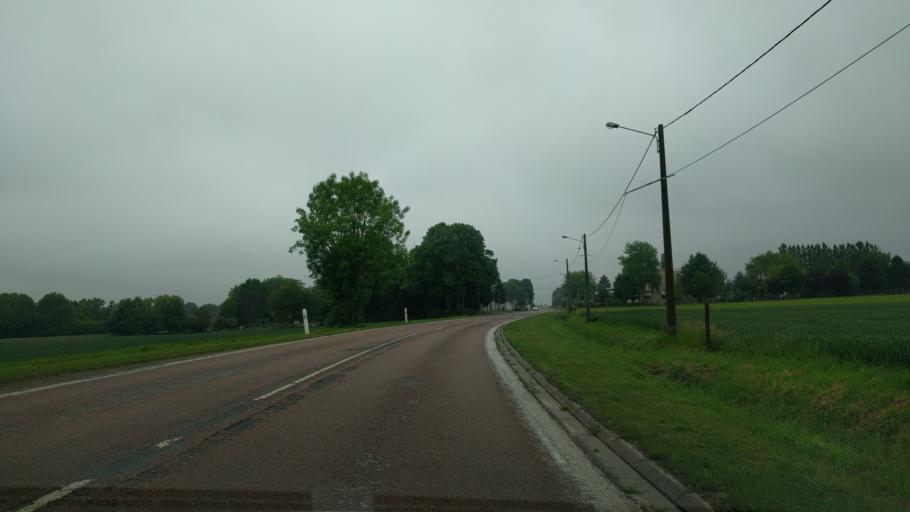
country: FR
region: Picardie
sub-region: Departement de la Somme
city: Moislains
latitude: 50.0009
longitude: 2.9096
